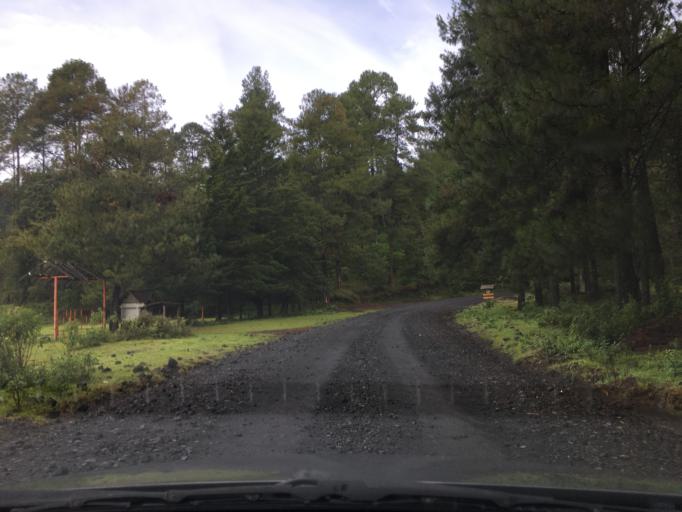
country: MX
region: Michoacan
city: Nuevo San Juan Parangaricutiro
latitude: 19.4586
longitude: -102.1952
